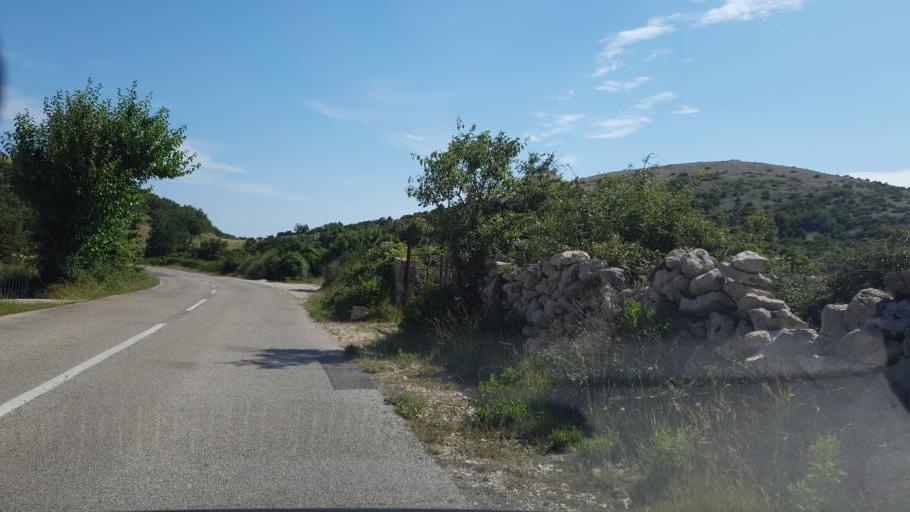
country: HR
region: Primorsko-Goranska
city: Punat
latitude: 44.9866
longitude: 14.6484
